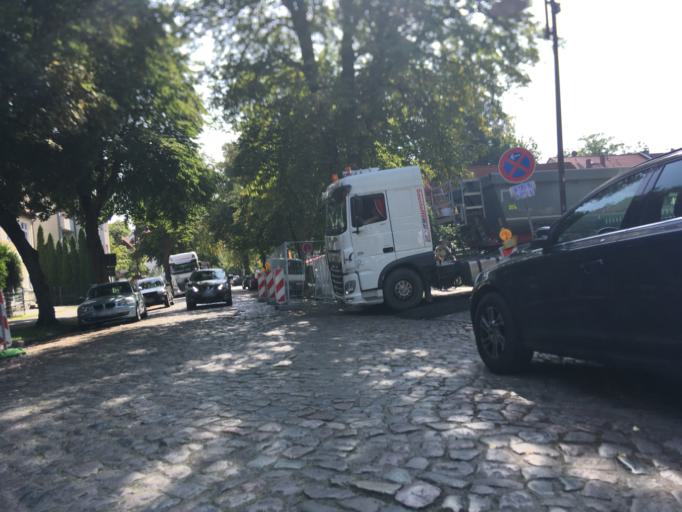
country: DE
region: Brandenburg
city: Zeuthen
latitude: 52.3748
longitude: 13.6193
